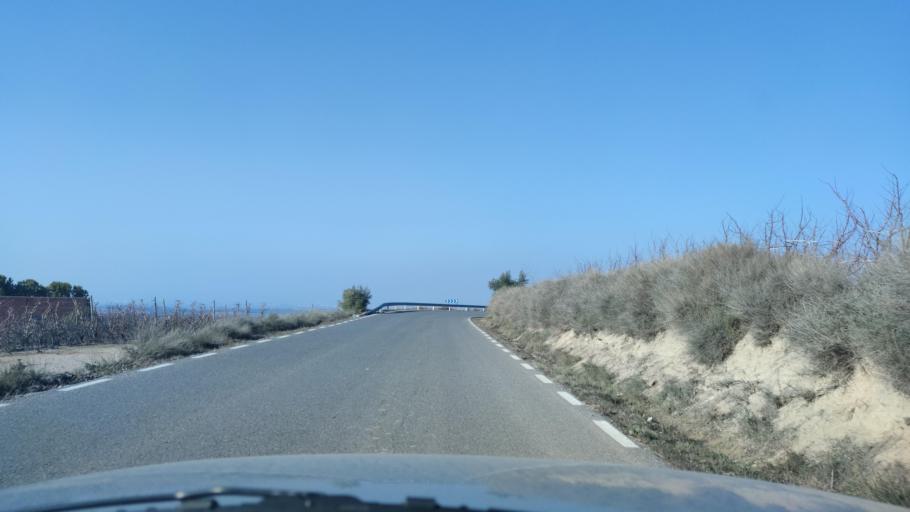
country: ES
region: Catalonia
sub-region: Provincia de Lleida
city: Sunyer
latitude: 41.5199
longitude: 0.5641
